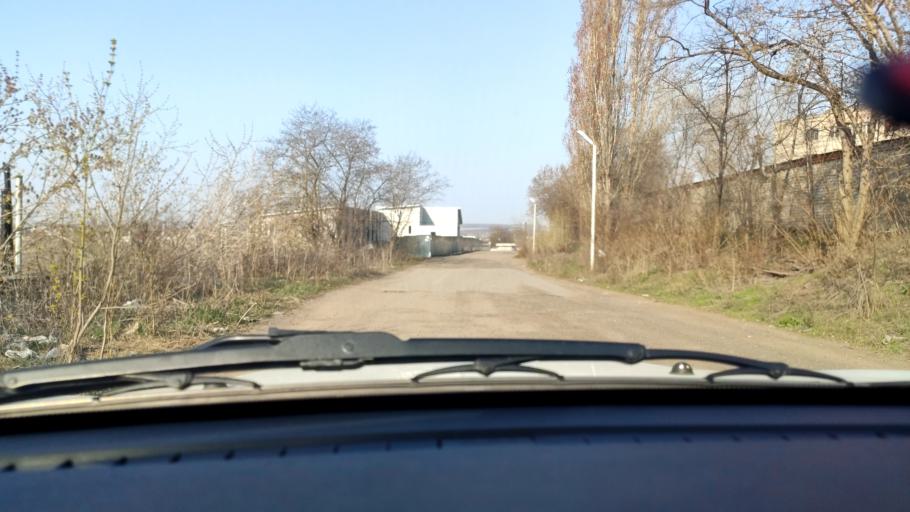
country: RU
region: Voronezj
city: Voronezh
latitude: 51.6399
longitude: 39.1267
